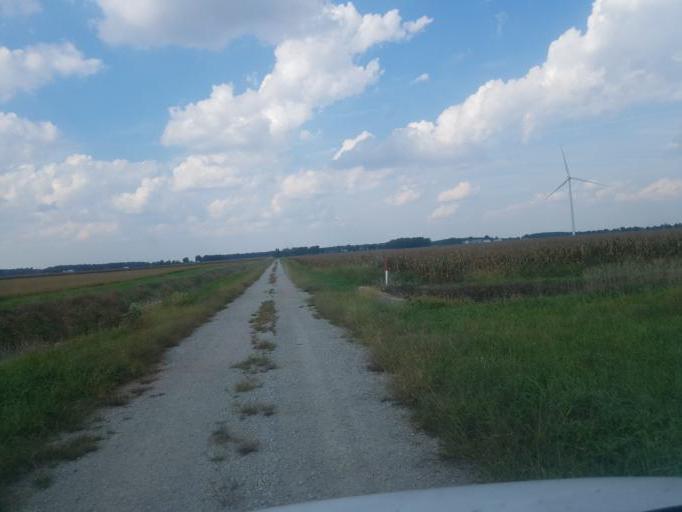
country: US
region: Ohio
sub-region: Hancock County
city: Arlington
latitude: 40.7979
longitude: -83.6898
